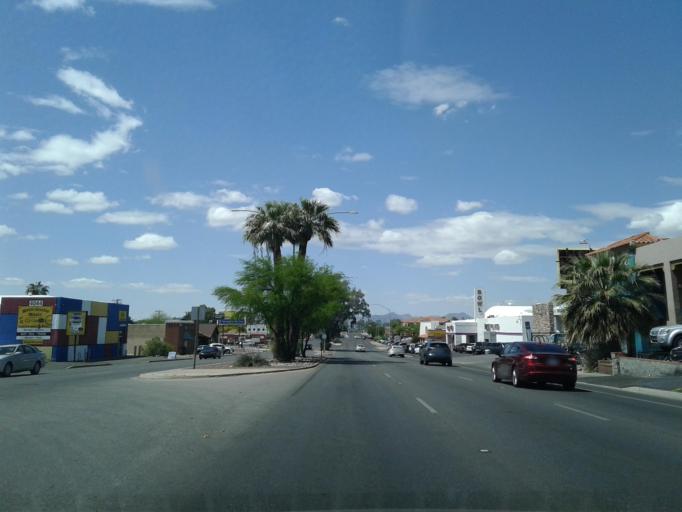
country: US
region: Arizona
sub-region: Pima County
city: Tucson
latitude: 32.2363
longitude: -110.9052
